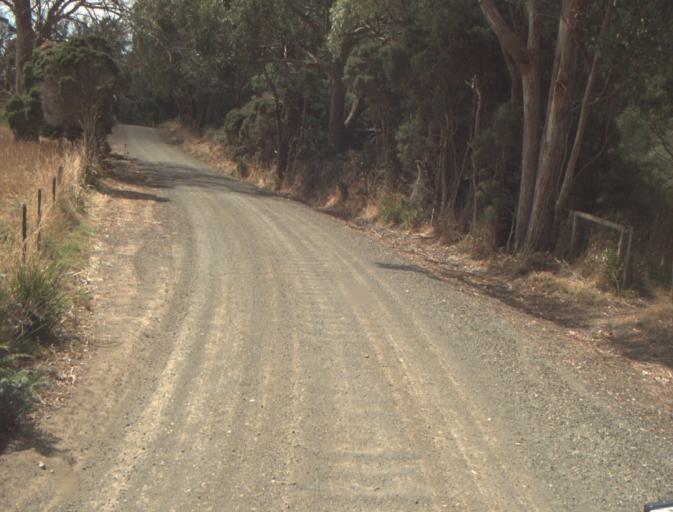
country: AU
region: Tasmania
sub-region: Launceston
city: Mayfield
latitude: -41.3035
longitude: 146.9953
